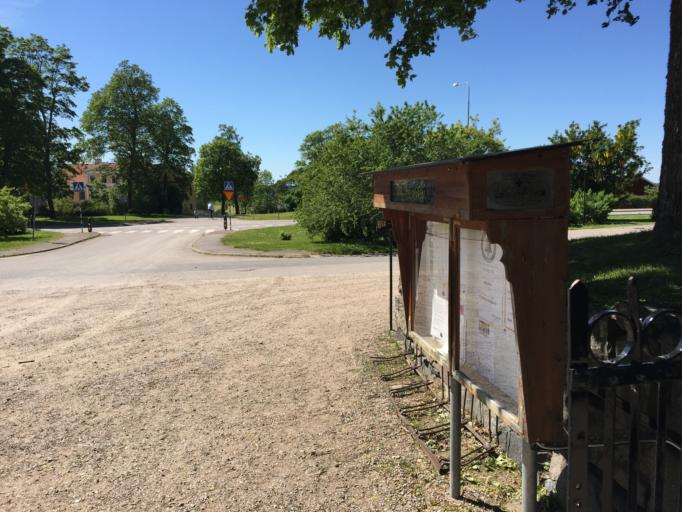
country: SE
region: Soedermanland
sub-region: Vingakers Kommun
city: Vingaker
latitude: 59.0525
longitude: 15.8785
